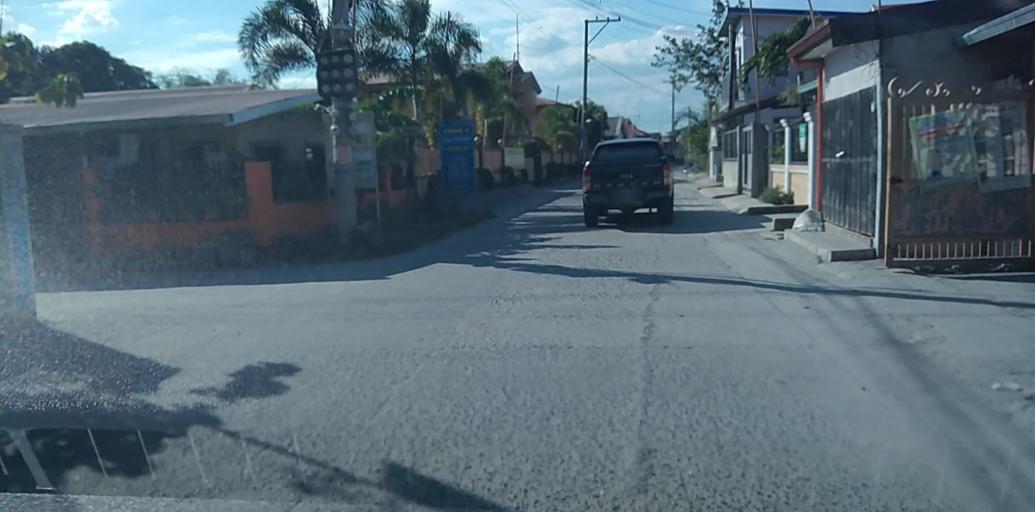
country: PH
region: Central Luzon
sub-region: Province of Pampanga
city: Acli
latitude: 15.1068
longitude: 120.6567
